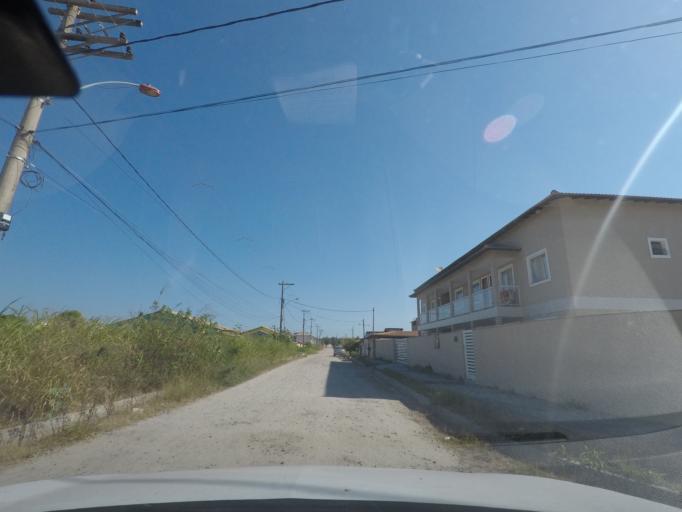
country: BR
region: Rio de Janeiro
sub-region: Marica
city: Marica
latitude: -22.9644
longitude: -42.9244
